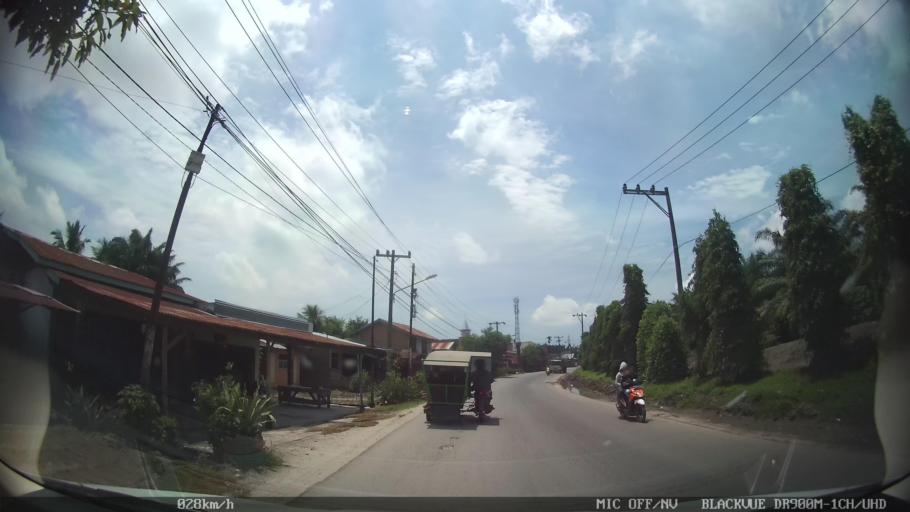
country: ID
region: North Sumatra
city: Perbaungan
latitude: 3.5351
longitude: 98.8853
